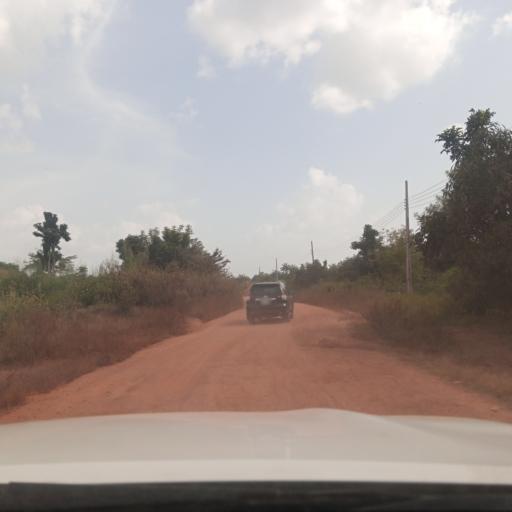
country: NG
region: Osun
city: Ede
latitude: 7.6722
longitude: 4.4681
